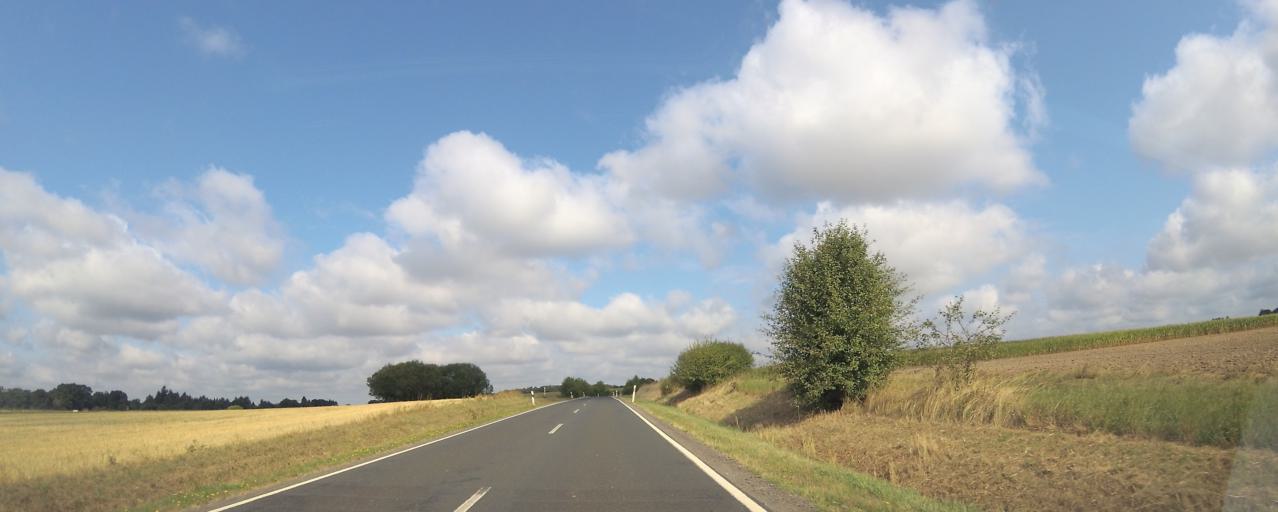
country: DE
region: Rheinland-Pfalz
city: Herforst
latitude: 49.9507
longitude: 6.6876
